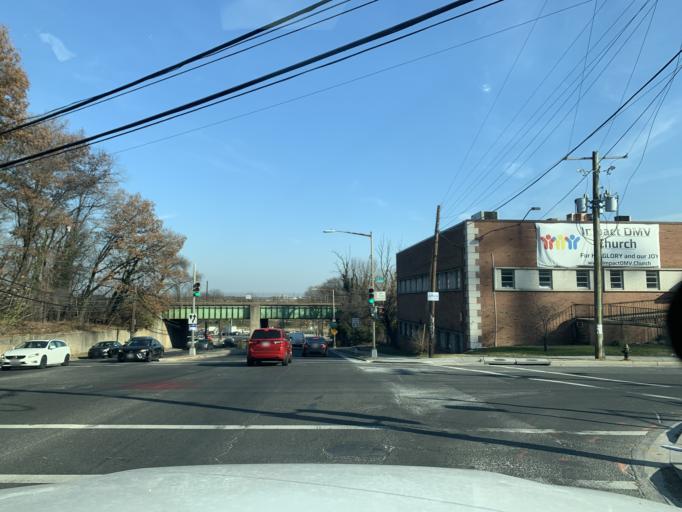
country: US
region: Maryland
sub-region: Prince George's County
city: Chillum
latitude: 38.9557
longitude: -77.0049
